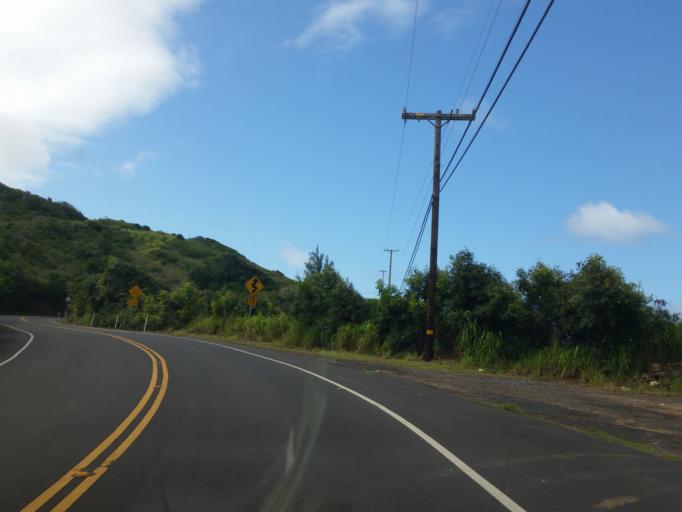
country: US
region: Hawaii
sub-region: Maui County
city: Waihee-Waiehu
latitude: 20.9483
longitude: -156.5178
